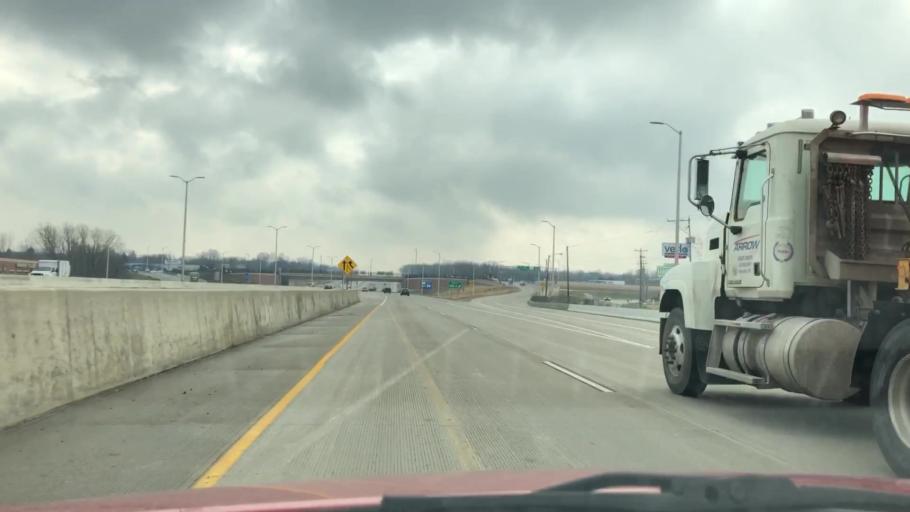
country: US
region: Wisconsin
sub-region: Brown County
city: Howard
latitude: 44.5282
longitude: -88.0820
